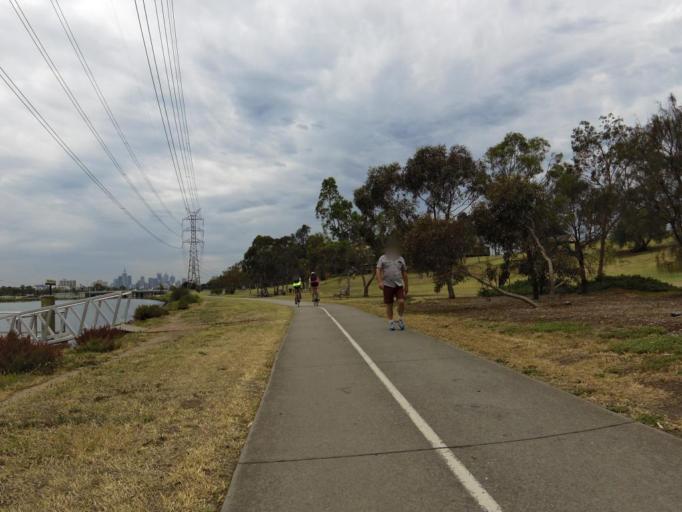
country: AU
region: Victoria
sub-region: Maribyrnong
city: Footscray
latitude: -37.7937
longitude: 144.9075
